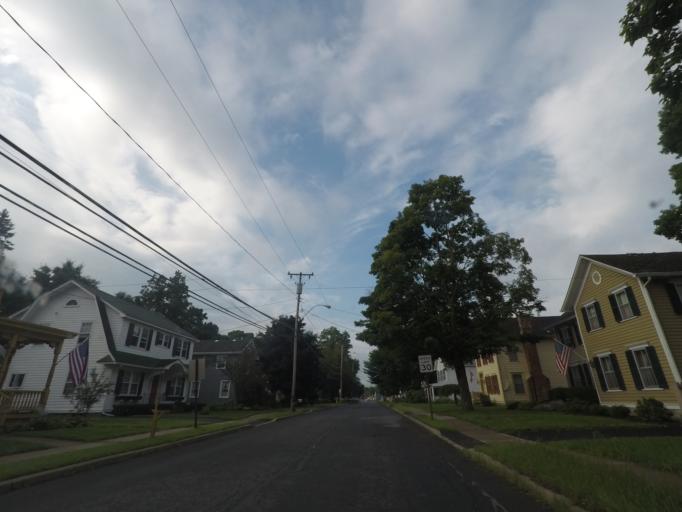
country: US
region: New York
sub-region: Rensselaer County
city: Nassau
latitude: 42.5190
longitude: -73.6088
